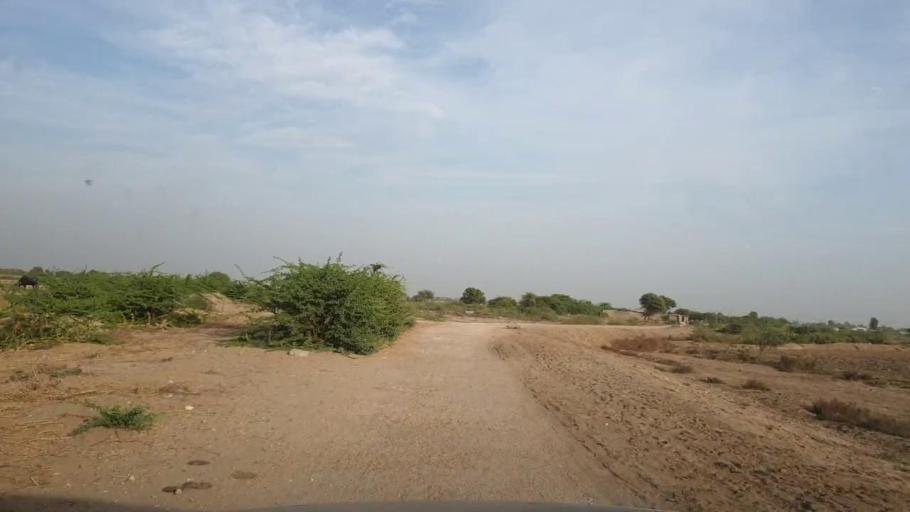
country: PK
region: Sindh
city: Kunri
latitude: 25.2255
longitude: 69.5129
